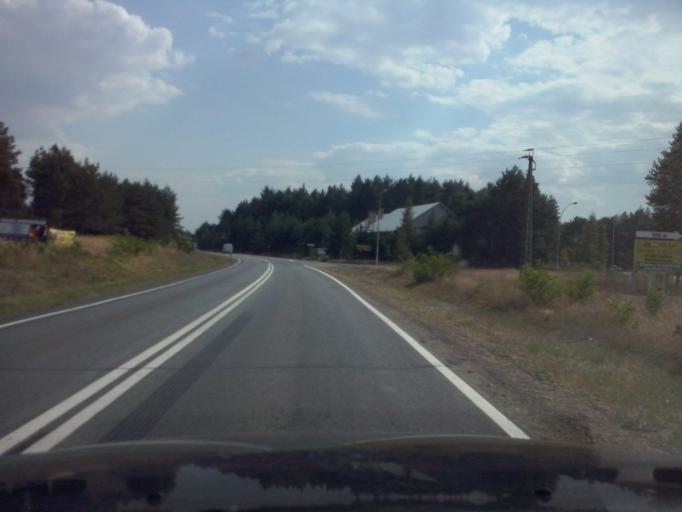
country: PL
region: Subcarpathian Voivodeship
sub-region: Powiat nizanski
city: Rudnik nad Sanem
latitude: 50.4549
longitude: 22.2429
